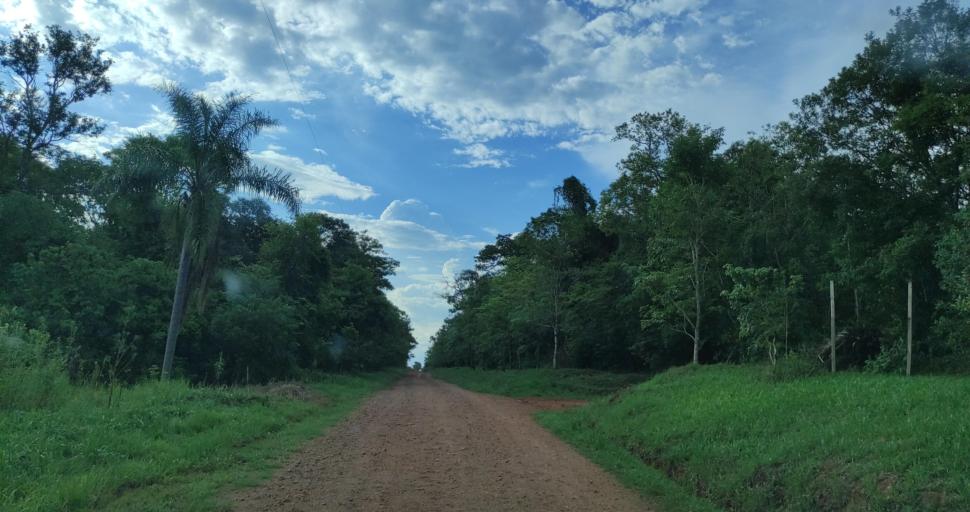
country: AR
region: Misiones
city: Gobernador Roca
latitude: -27.1821
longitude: -55.4667
